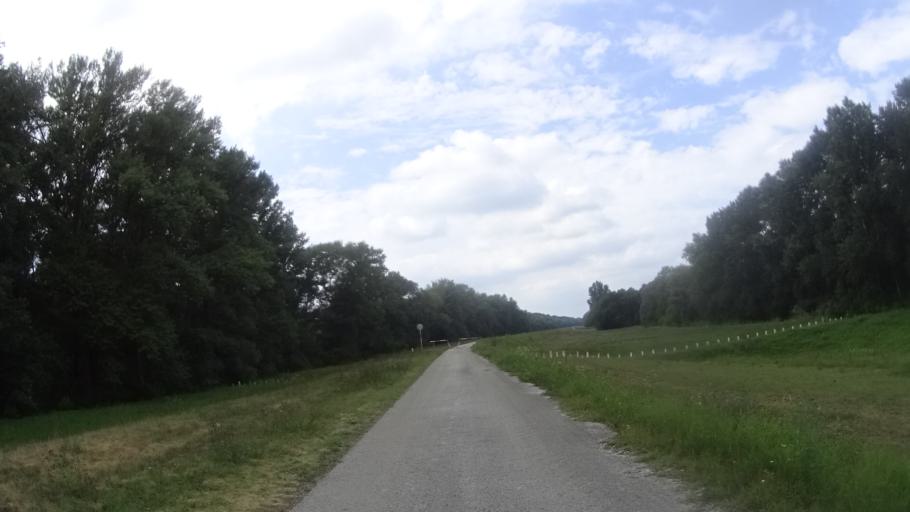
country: SK
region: Trnavsky
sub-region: Okres Dunajska Streda
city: Velky Meder
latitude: 47.7683
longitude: 17.7202
